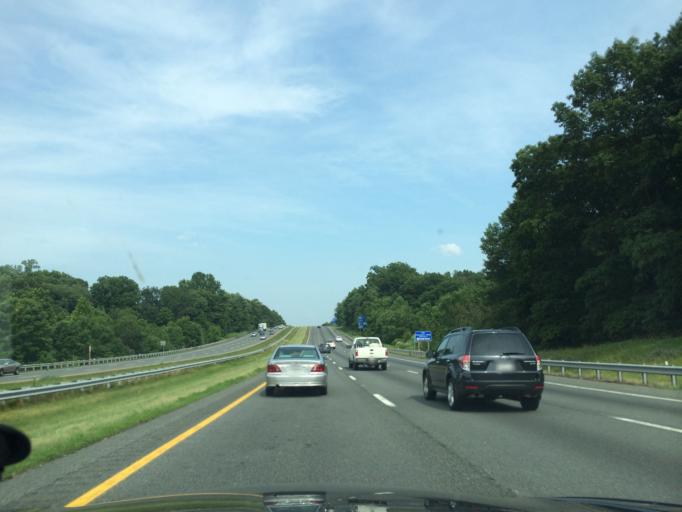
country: US
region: Maryland
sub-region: Frederick County
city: Spring Ridge
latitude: 39.3852
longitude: -77.2941
